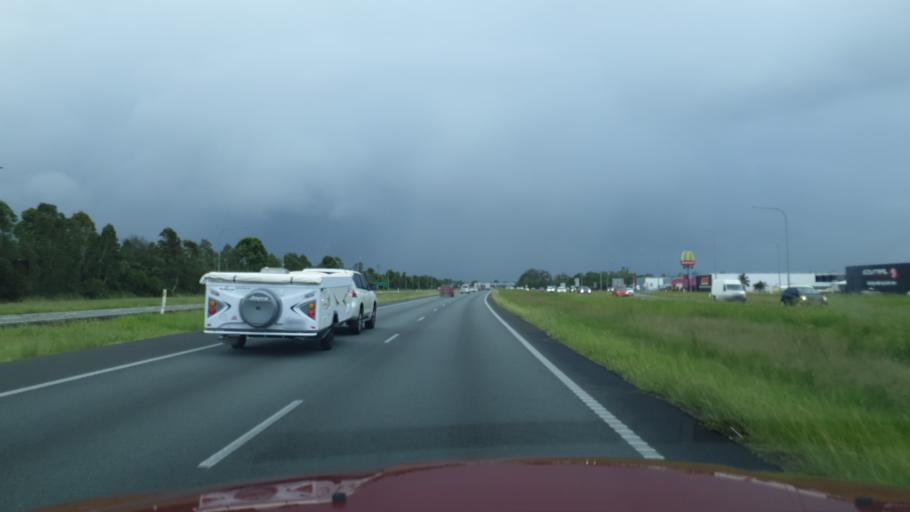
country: AU
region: Queensland
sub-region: Moreton Bay
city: Caboolture
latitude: -27.0818
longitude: 152.9749
